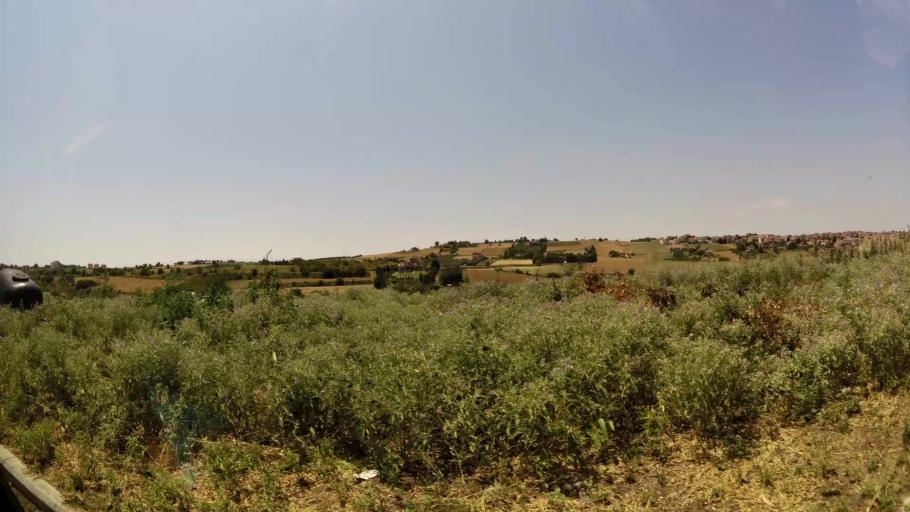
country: GR
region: Central Macedonia
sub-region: Nomos Thessalonikis
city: Trilofos
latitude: 40.4656
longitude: 22.9668
